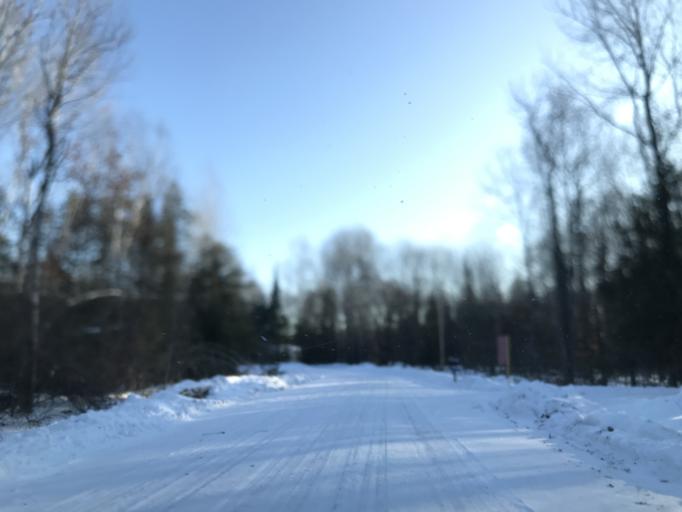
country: US
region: Michigan
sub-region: Menominee County
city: Menominee
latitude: 45.2904
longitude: -87.6967
